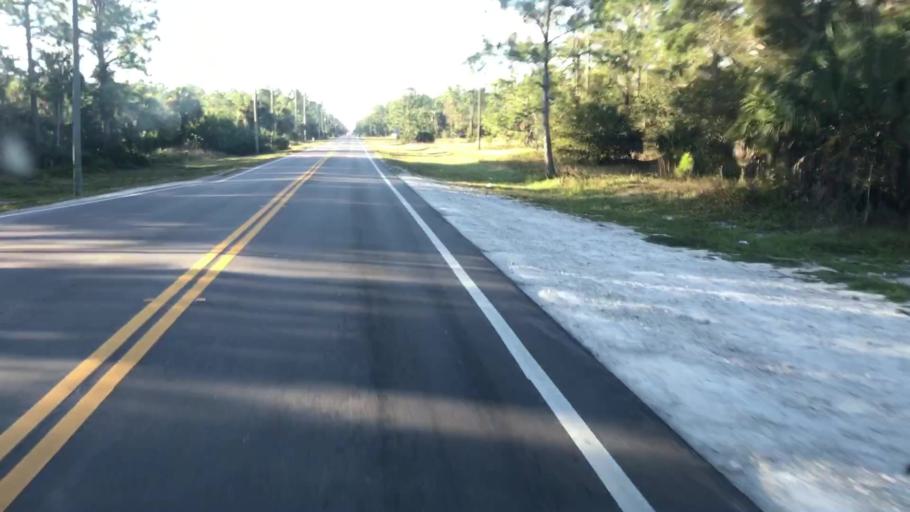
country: US
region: Florida
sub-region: Collier County
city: Orangetree
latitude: 26.2756
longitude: -81.6073
